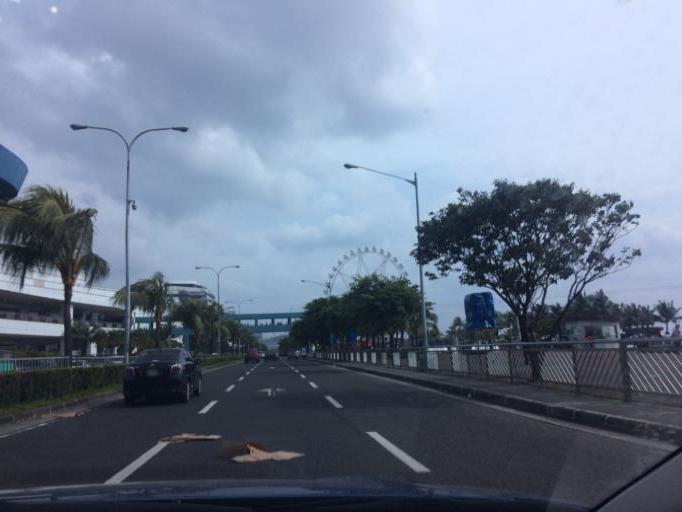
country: PH
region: Metro Manila
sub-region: City of Manila
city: Port Area
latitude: 14.5355
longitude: 120.9796
